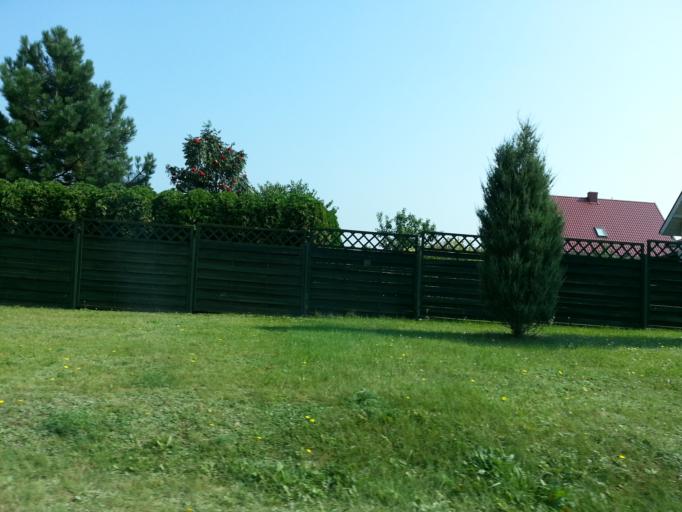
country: LT
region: Vilnius County
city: Pasilaiciai
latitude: 54.7301
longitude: 25.2060
